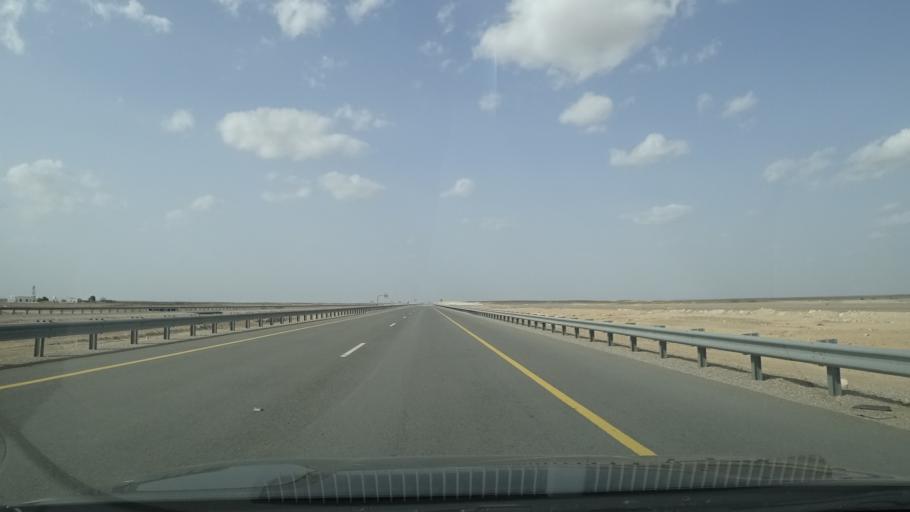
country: OM
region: Muhafazat ad Dakhiliyah
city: Adam
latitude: 22.0201
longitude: 57.4943
